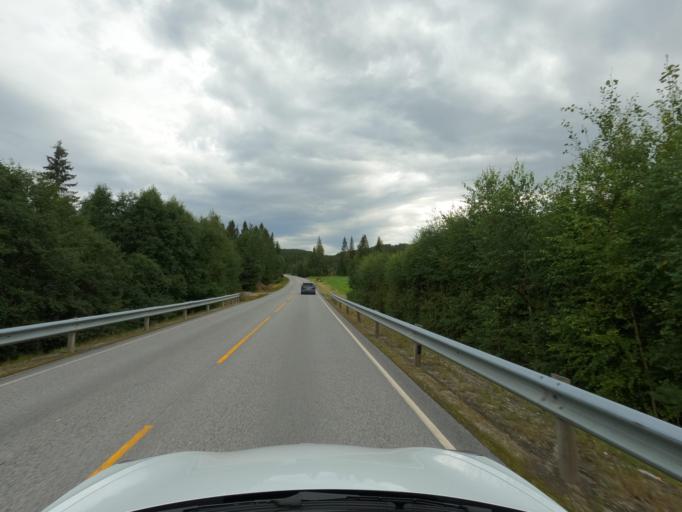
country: NO
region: Telemark
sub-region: Hjartdal
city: Sauland
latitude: 59.7028
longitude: 9.0124
